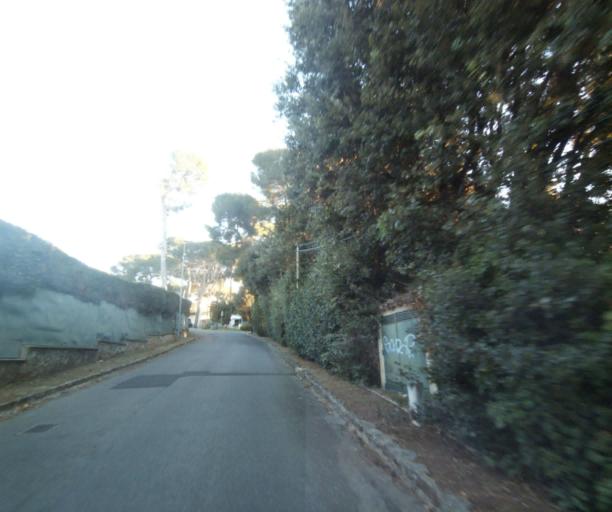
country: FR
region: Provence-Alpes-Cote d'Azur
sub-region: Departement des Alpes-Maritimes
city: Vallauris
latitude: 43.5806
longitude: 7.0847
